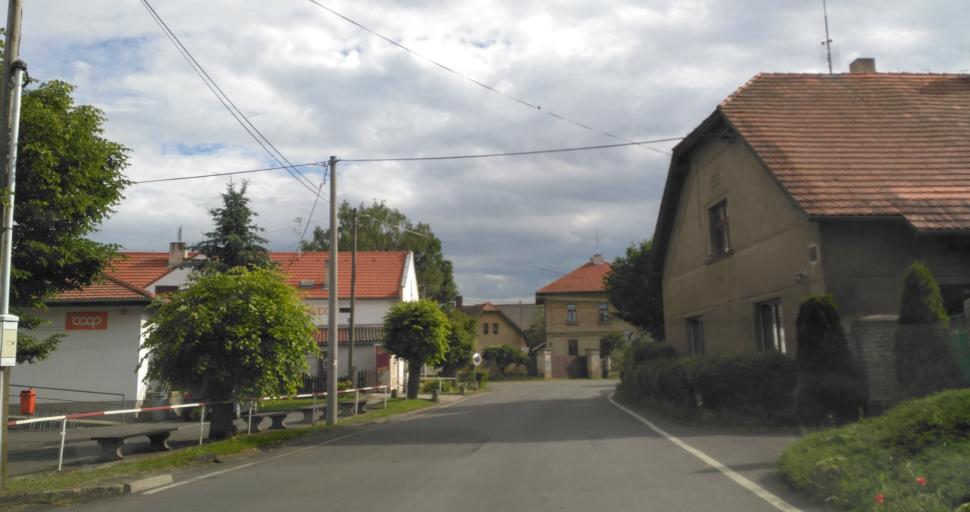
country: CZ
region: Central Bohemia
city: Hostomice
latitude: 49.8837
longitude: 14.0638
